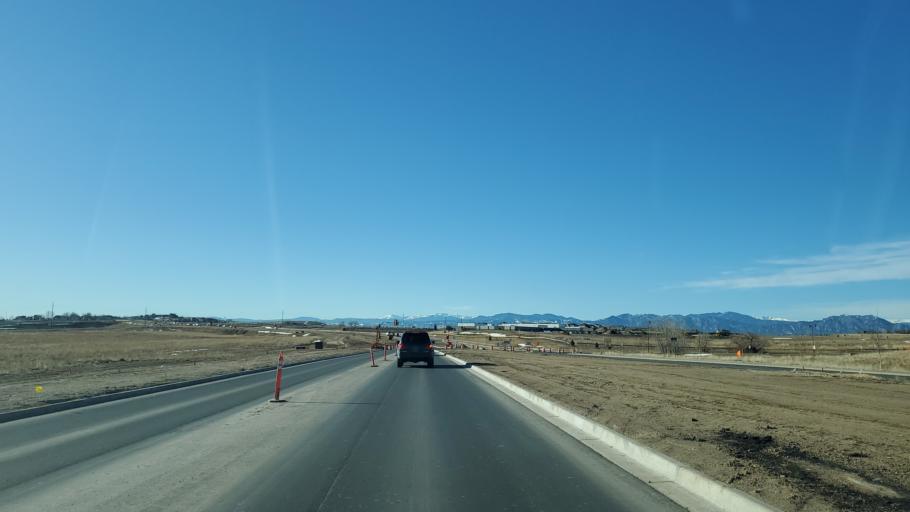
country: US
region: Colorado
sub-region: Boulder County
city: Erie
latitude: 39.9927
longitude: -105.0126
